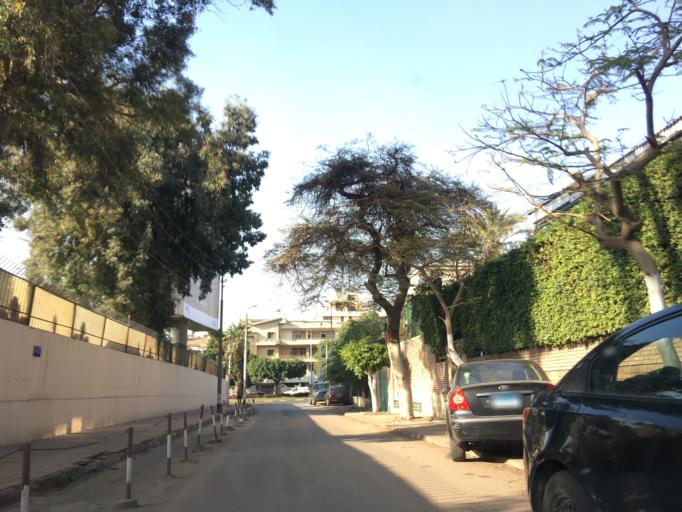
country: EG
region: Muhafazat al Qahirah
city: Cairo
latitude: 30.0867
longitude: 31.3283
